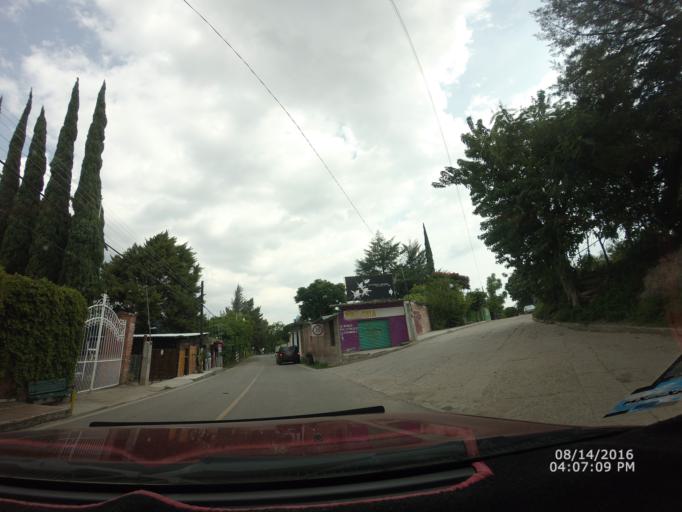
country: MX
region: Oaxaca
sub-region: San Juan Bautista Guelache
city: Fraccionamiento San Miguel
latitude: 17.1928
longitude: -96.7645
